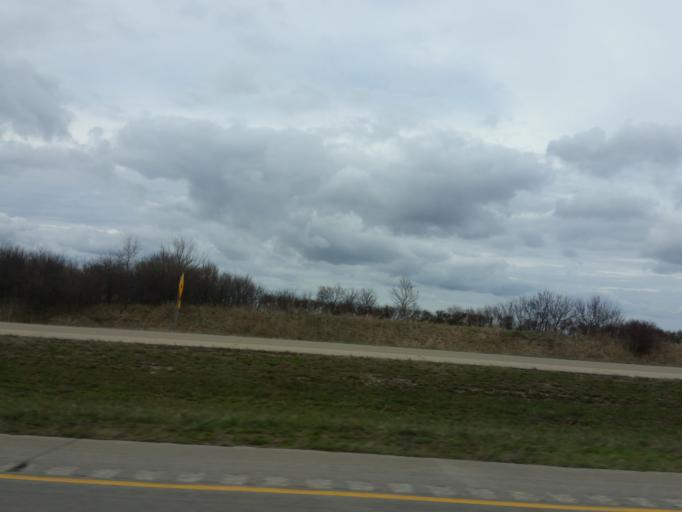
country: US
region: Iowa
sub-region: Black Hawk County
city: Elk Run Heights
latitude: 42.4492
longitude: -92.2049
